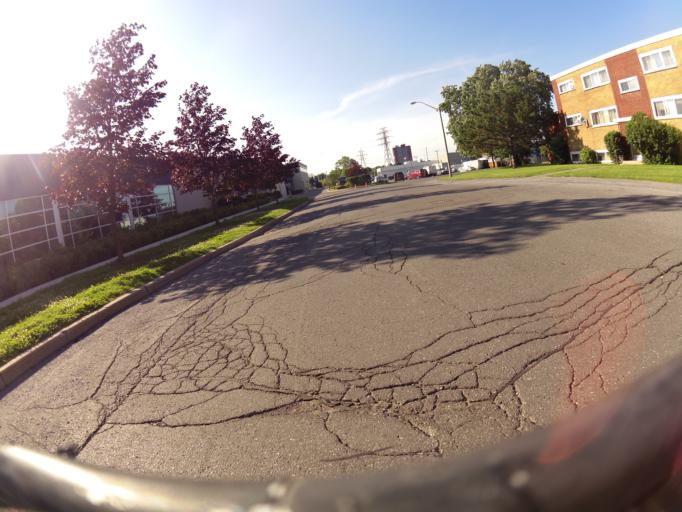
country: CA
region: Ontario
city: Ottawa
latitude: 45.3798
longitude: -75.7407
